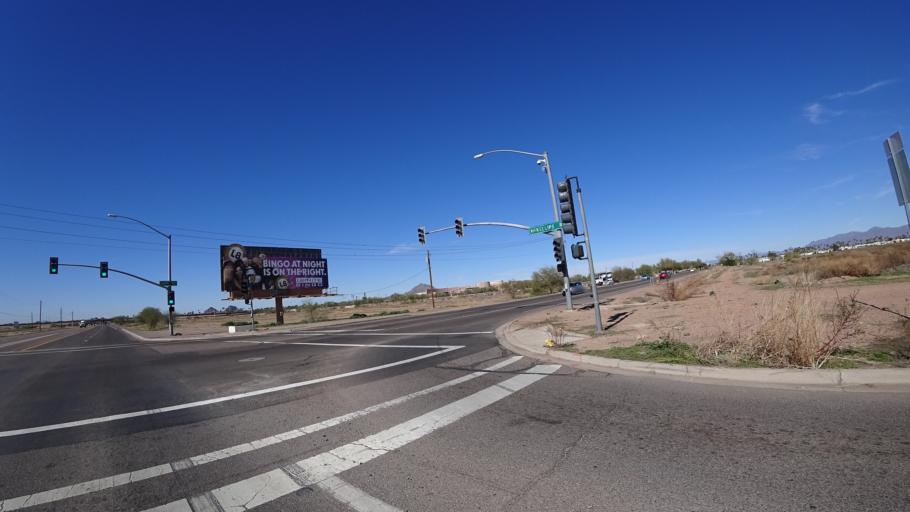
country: US
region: Arizona
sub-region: Maricopa County
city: Tempe
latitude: 33.4514
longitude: -111.8831
